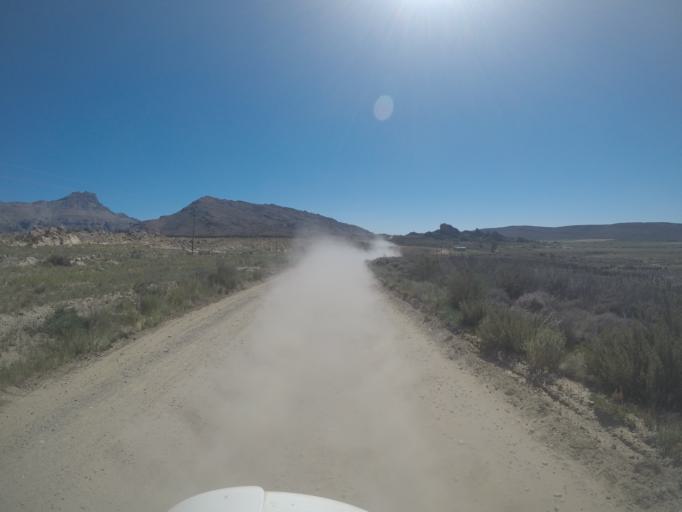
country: ZA
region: Western Cape
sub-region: Cape Winelands District Municipality
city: Ceres
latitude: -32.8622
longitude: 19.4433
